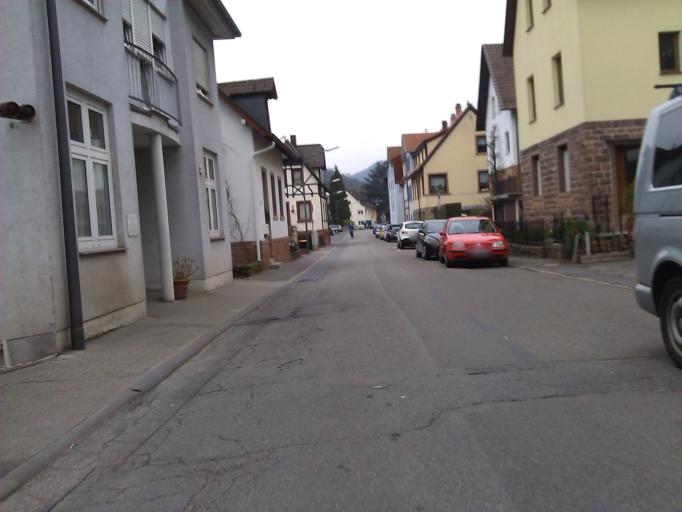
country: DE
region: Baden-Wuerttemberg
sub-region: Karlsruhe Region
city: Gaiberg
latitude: 49.4174
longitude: 8.7483
